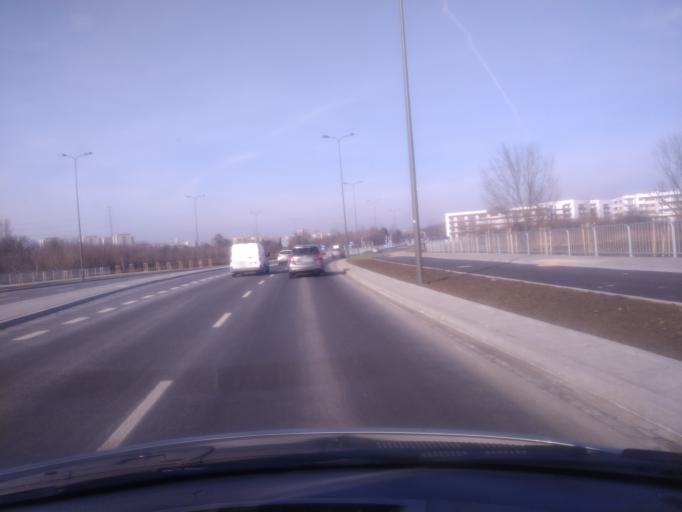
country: PL
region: Masovian Voivodeship
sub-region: Warszawa
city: Mokotow
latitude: 52.2046
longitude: 21.0663
